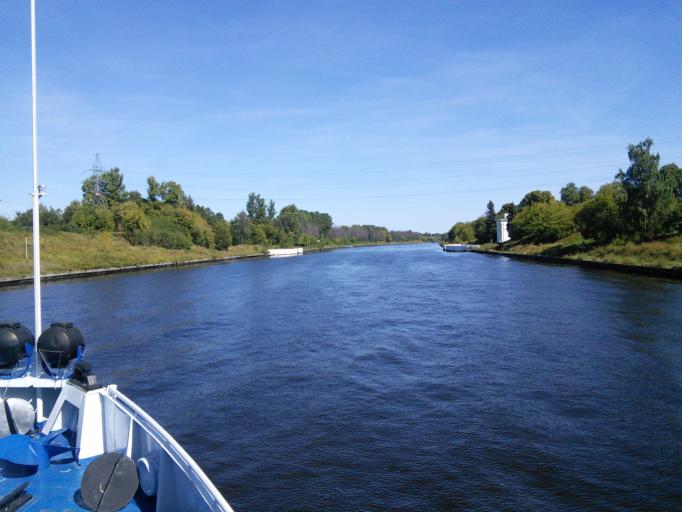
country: RU
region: Moskovskaya
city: Dolgoprudnyy
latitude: 55.9479
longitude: 37.4796
